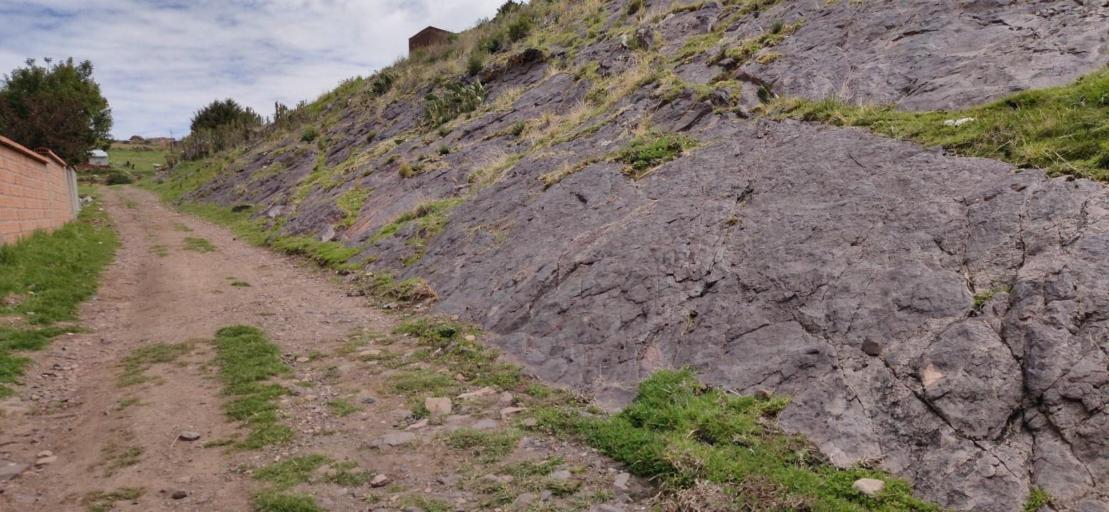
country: BO
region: La Paz
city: Batallas
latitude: -16.3462
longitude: -68.6371
